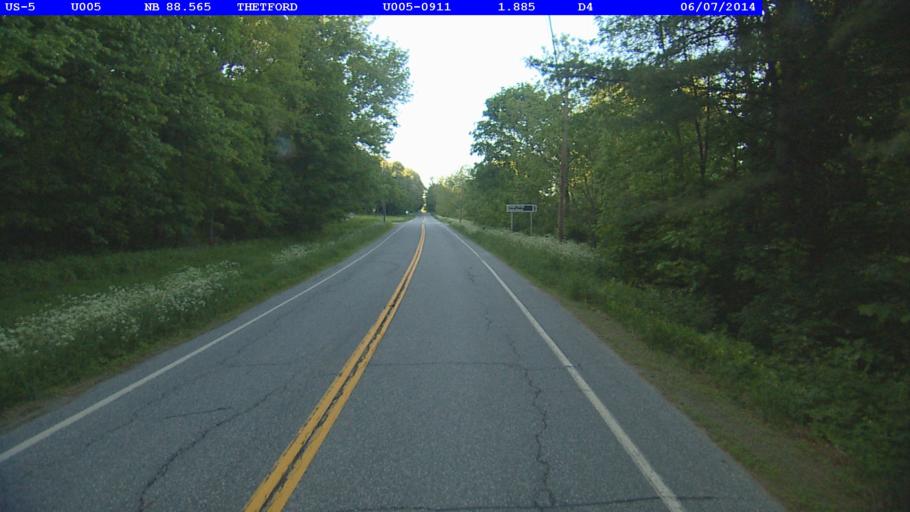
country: US
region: New Hampshire
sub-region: Grafton County
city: Lyme
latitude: 43.7965
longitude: -72.1956
